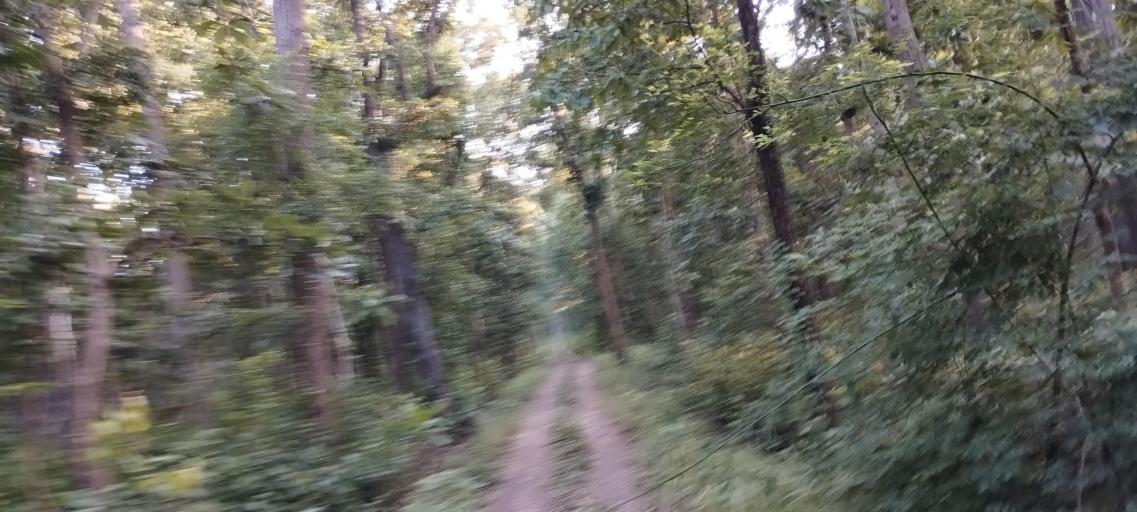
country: NP
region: Far Western
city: Tikapur
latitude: 28.4906
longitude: 81.2656
